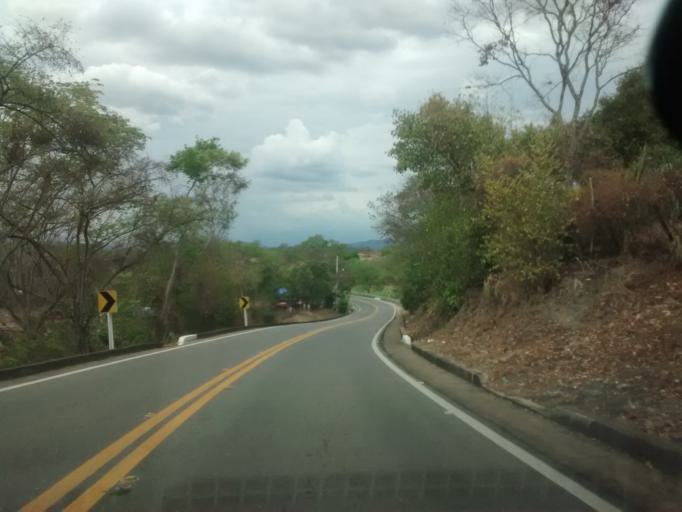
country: CO
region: Cundinamarca
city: Agua de Dios
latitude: 4.4189
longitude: -74.7064
